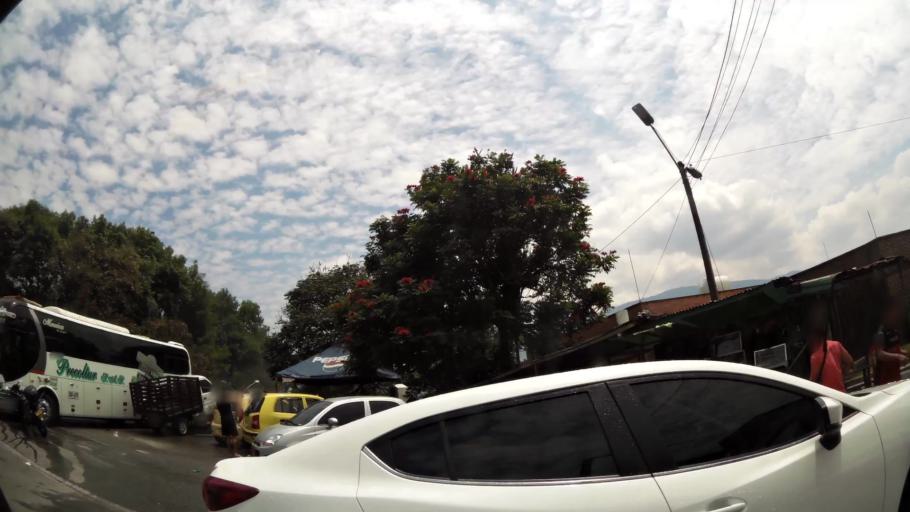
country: CO
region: Antioquia
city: Bello
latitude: 6.3027
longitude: -75.5793
